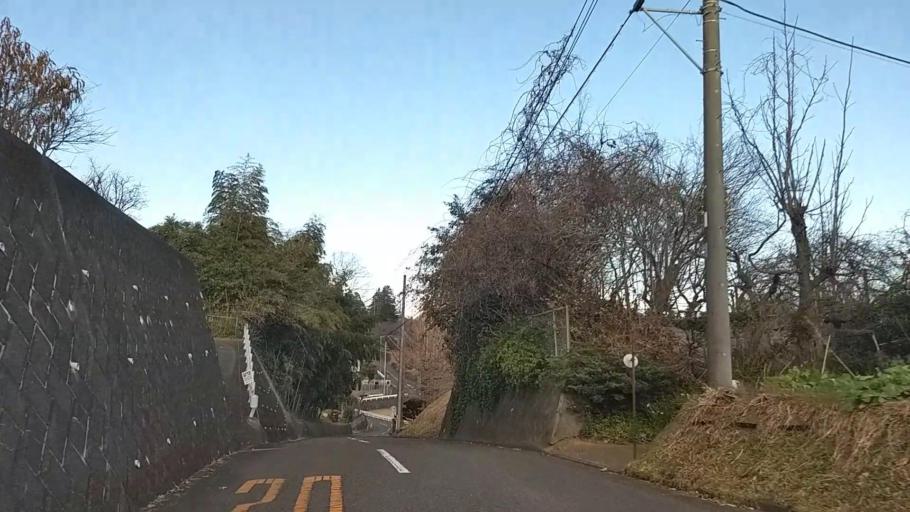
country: JP
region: Kanagawa
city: Isehara
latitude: 35.4272
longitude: 139.3146
